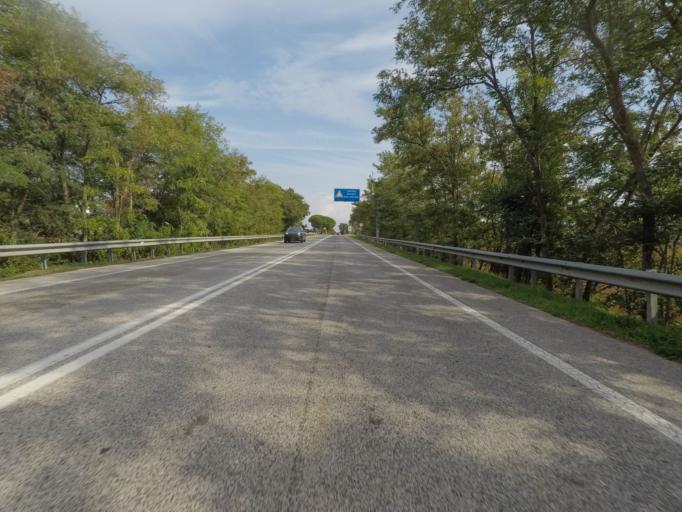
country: IT
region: Tuscany
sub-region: Provincia di Grosseto
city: Capalbio
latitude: 42.4144
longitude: 11.4425
